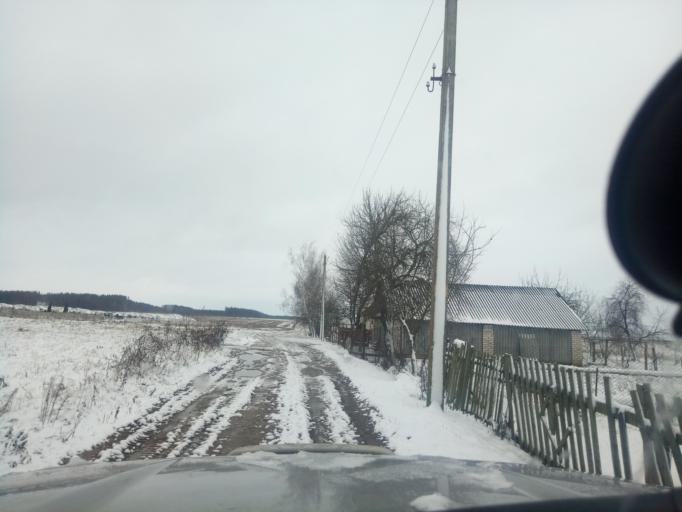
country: BY
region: Minsk
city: Klyetsk
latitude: 53.0227
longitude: 26.7157
